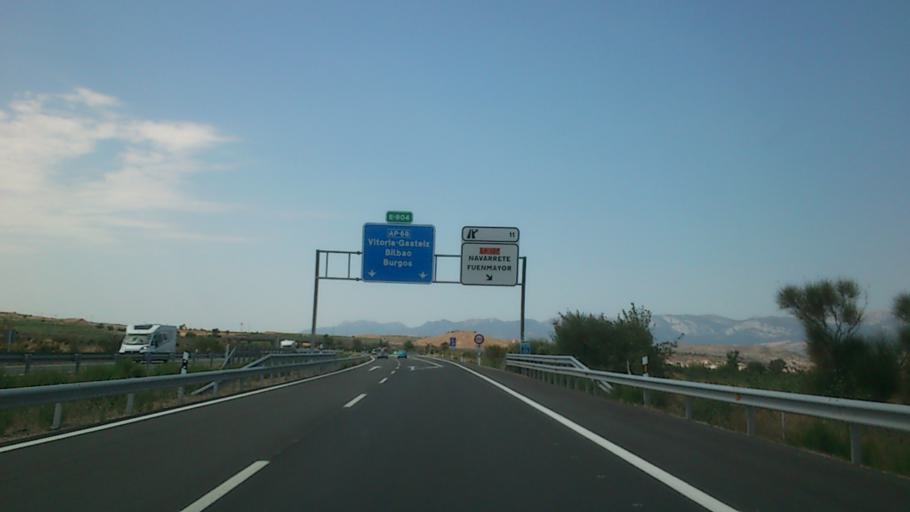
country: ES
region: La Rioja
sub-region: Provincia de La Rioja
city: Navarrete
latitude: 42.4418
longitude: -2.5564
